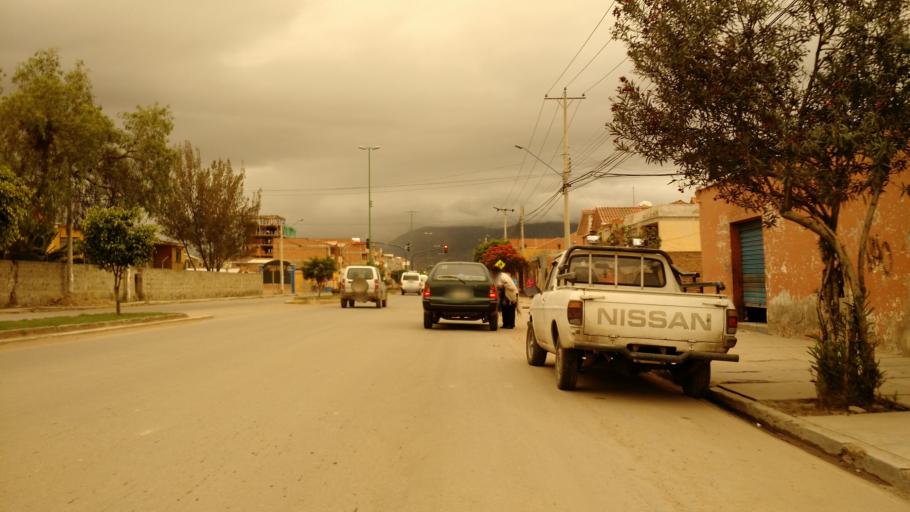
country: BO
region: Cochabamba
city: Cochabamba
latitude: -17.4214
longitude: -66.1666
